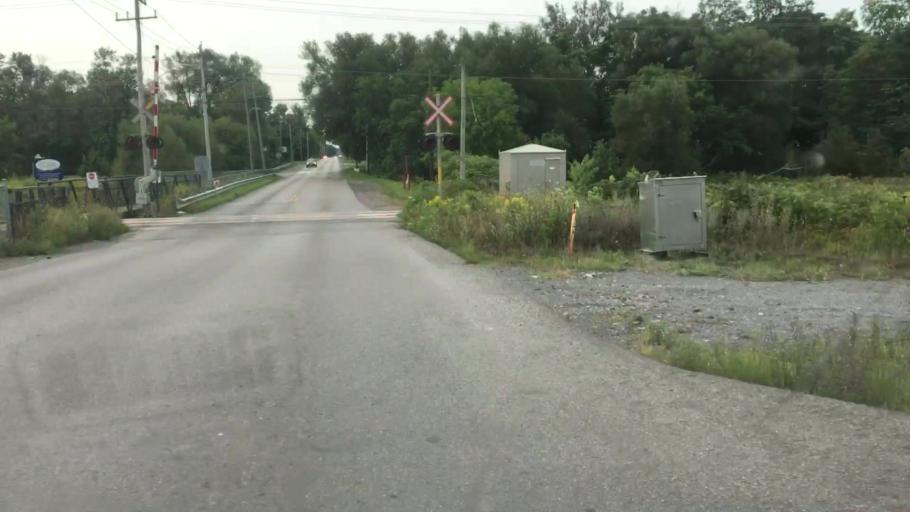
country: CA
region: Ontario
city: Quinte West
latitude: 44.0351
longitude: -77.7446
